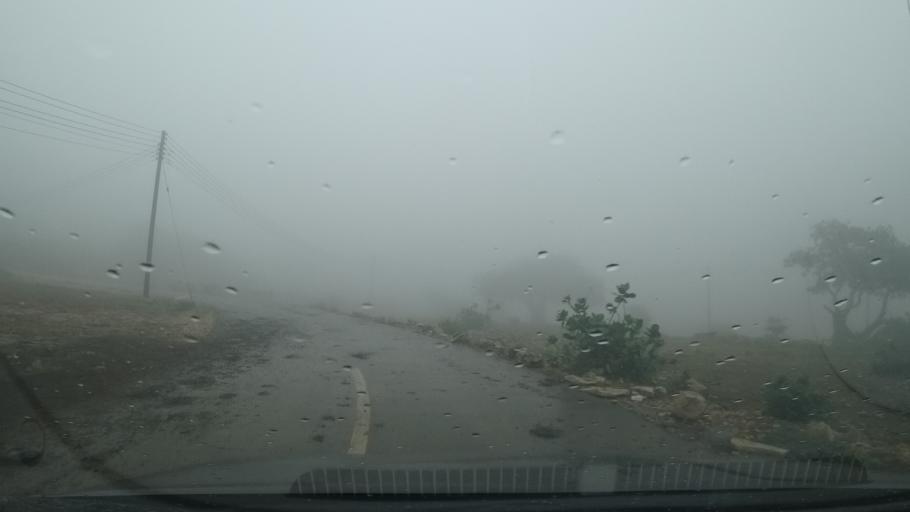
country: OM
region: Zufar
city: Salalah
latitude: 17.1155
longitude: 54.0140
